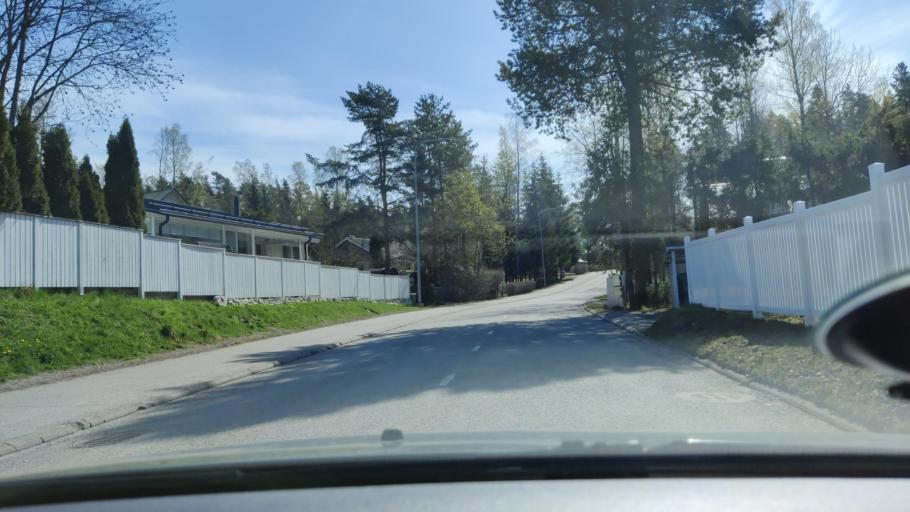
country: FI
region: Uusimaa
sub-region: Helsinki
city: Kerava
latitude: 60.3622
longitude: 25.0941
